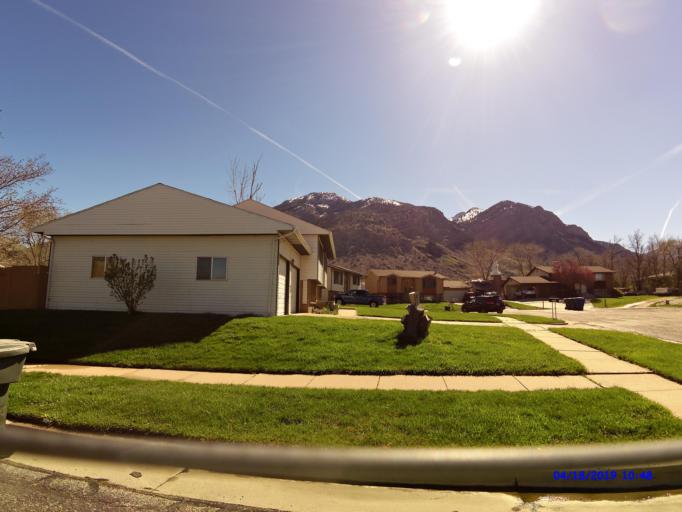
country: US
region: Utah
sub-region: Weber County
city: Harrisville
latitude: 41.2788
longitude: -111.9603
